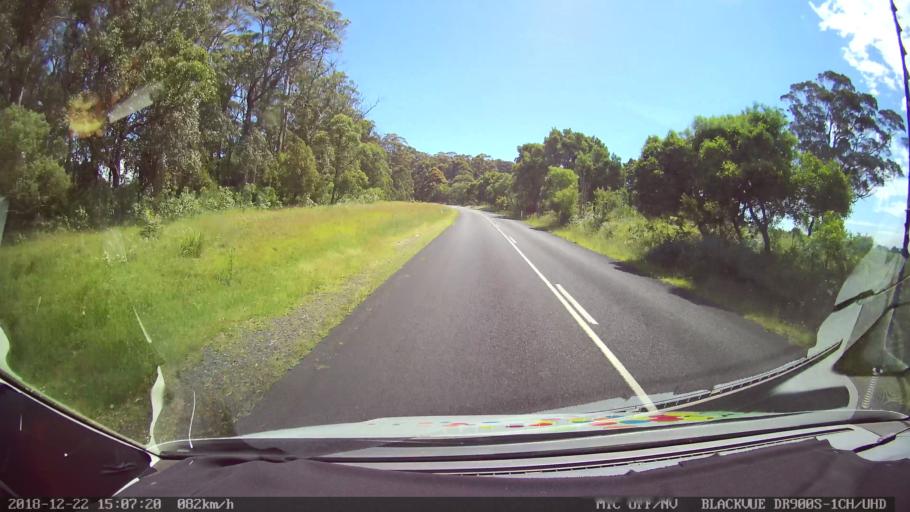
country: AU
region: New South Wales
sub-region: Bellingen
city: Dorrigo
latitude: -30.2992
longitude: 152.4160
